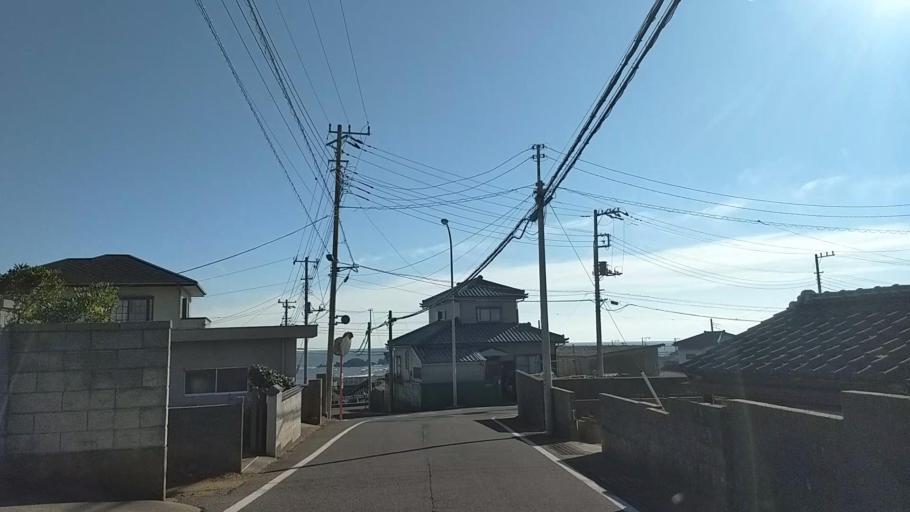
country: JP
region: Chiba
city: Hasaki
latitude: 35.6969
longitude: 140.8617
